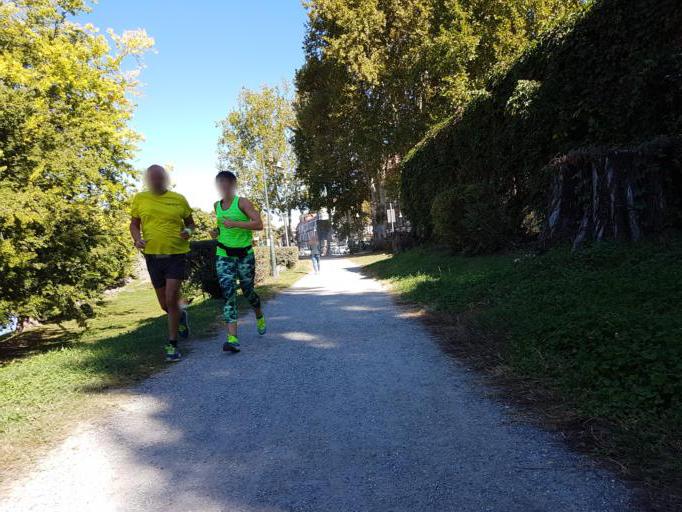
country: IT
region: Piedmont
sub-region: Provincia di Torino
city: Turin
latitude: 45.0566
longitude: 7.6921
